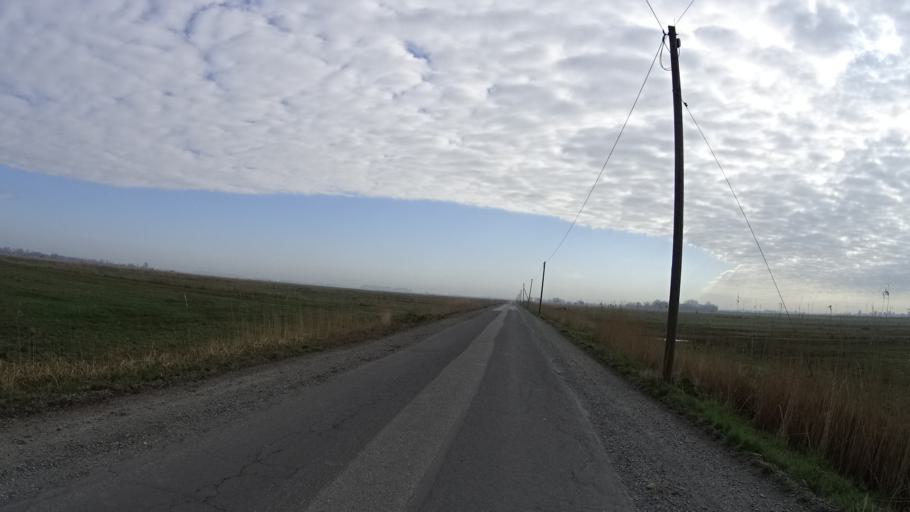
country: DE
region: Lower Saxony
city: Emden
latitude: 53.4032
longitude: 7.3074
